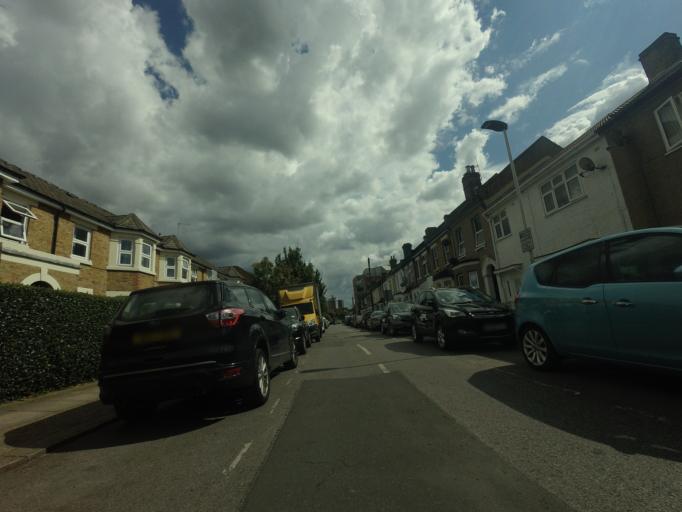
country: GB
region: England
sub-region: Greater London
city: Poplar
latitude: 51.5475
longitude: 0.0073
